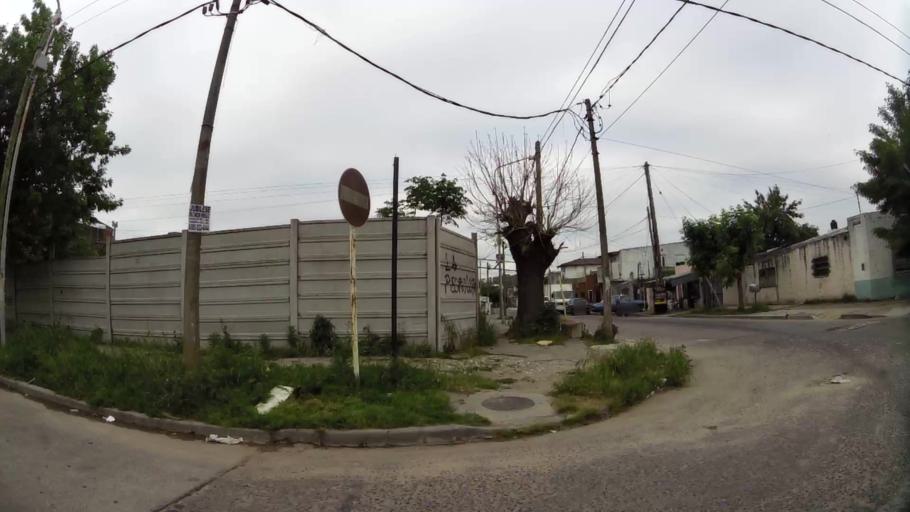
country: AR
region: Buenos Aires
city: San Justo
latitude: -34.7019
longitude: -58.5632
